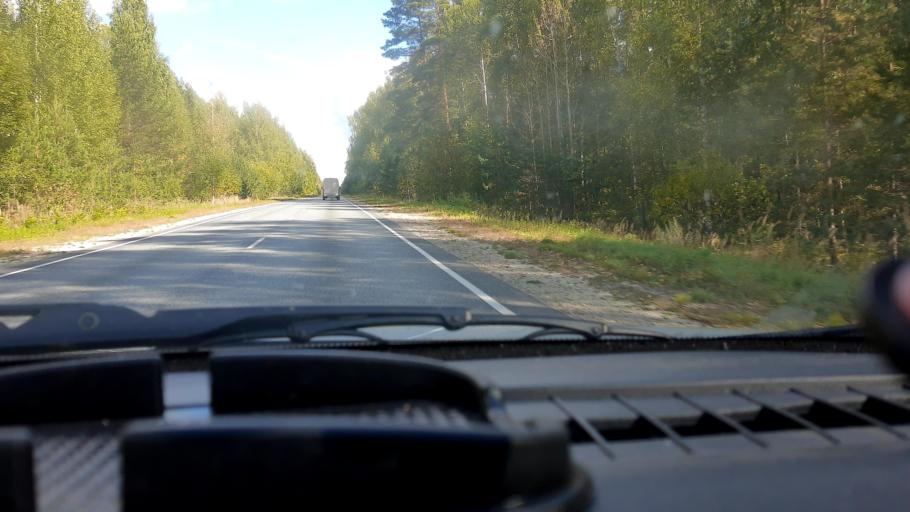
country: RU
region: Kirov
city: Sanchursk
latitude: 56.5751
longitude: 47.1869
